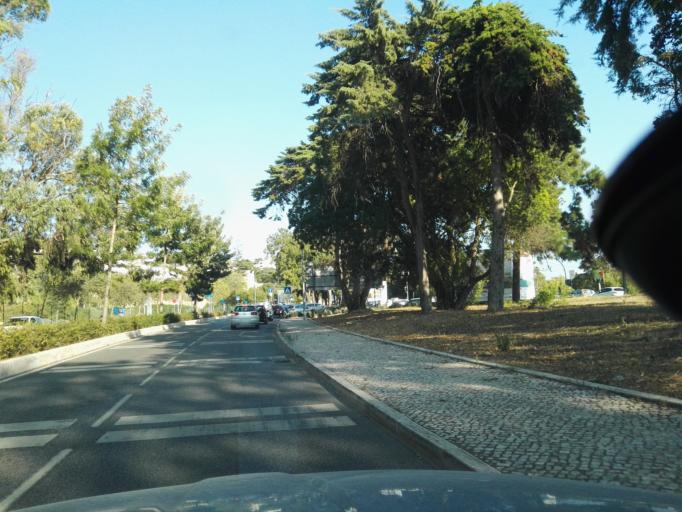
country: PT
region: Lisbon
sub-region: Oeiras
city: Linda-a-Velha
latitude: 38.7022
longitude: -9.2544
